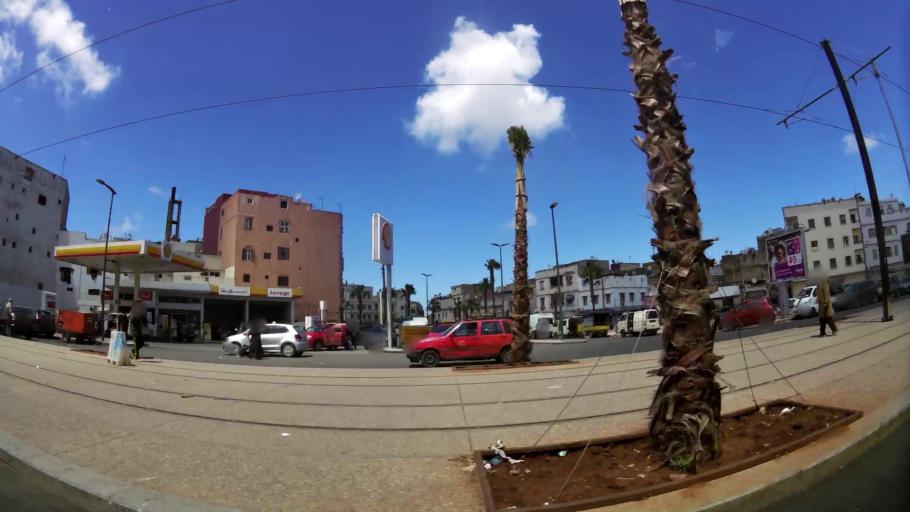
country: MA
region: Grand Casablanca
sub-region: Casablanca
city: Casablanca
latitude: 33.5692
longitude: -7.6029
